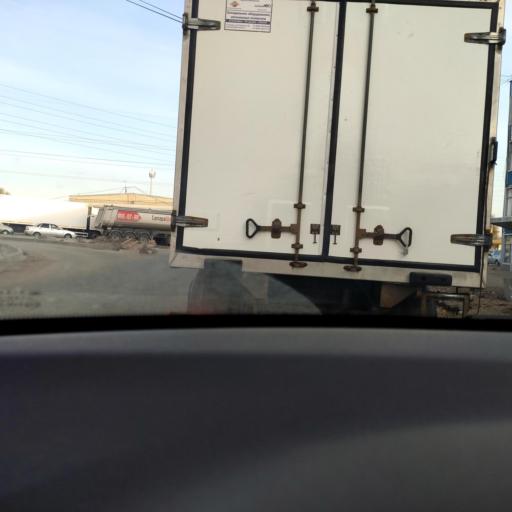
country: RU
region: Samara
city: Samara
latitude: 53.1943
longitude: 50.2457
